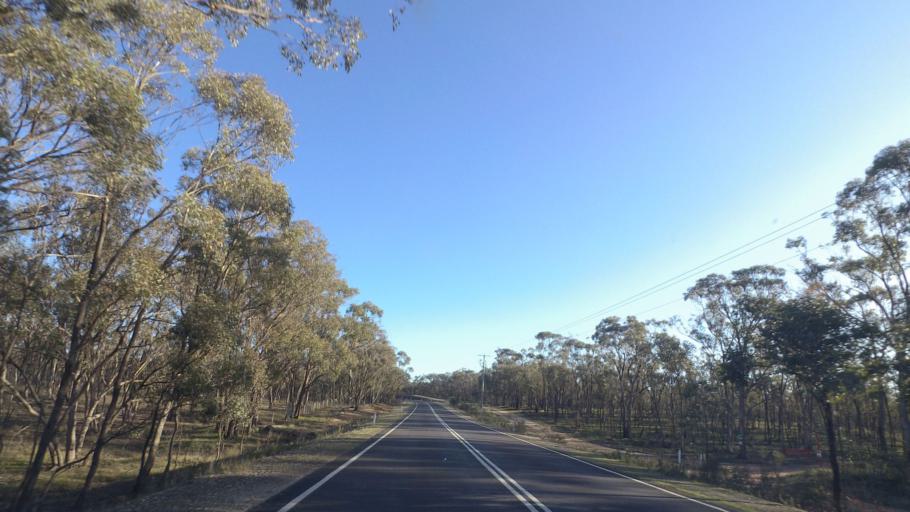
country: AU
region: Victoria
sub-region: Greater Bendigo
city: Kennington
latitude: -36.8749
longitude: 144.4954
